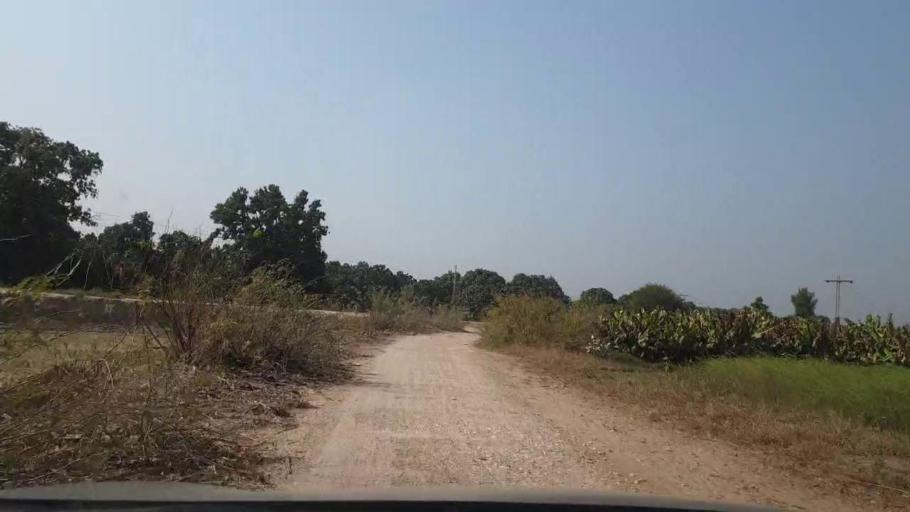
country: PK
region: Sindh
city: Tando Allahyar
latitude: 25.5259
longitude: 68.7551
